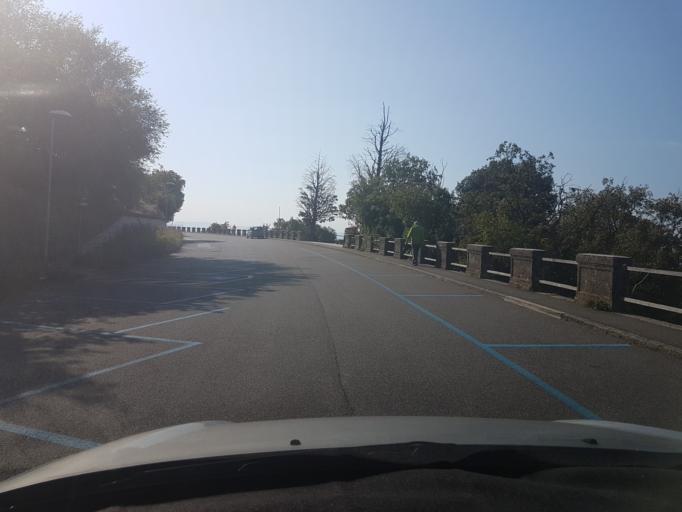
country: IT
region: Friuli Venezia Giulia
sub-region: Provincia di Trieste
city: Sistiana-Visogliano
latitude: 45.7623
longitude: 13.6393
